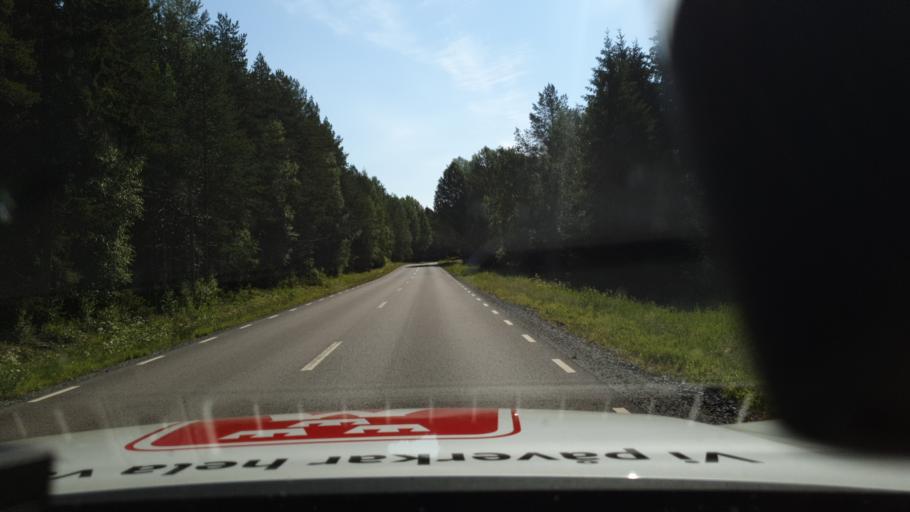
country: SE
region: Norrbotten
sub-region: Lulea Kommun
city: Sodra Sunderbyn
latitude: 65.8317
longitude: 21.9594
